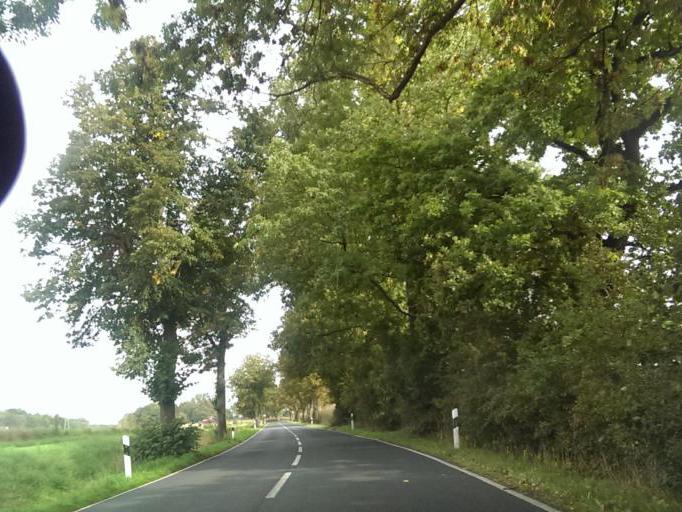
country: DE
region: Lower Saxony
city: Wunstorf
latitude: 52.4580
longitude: 9.4652
